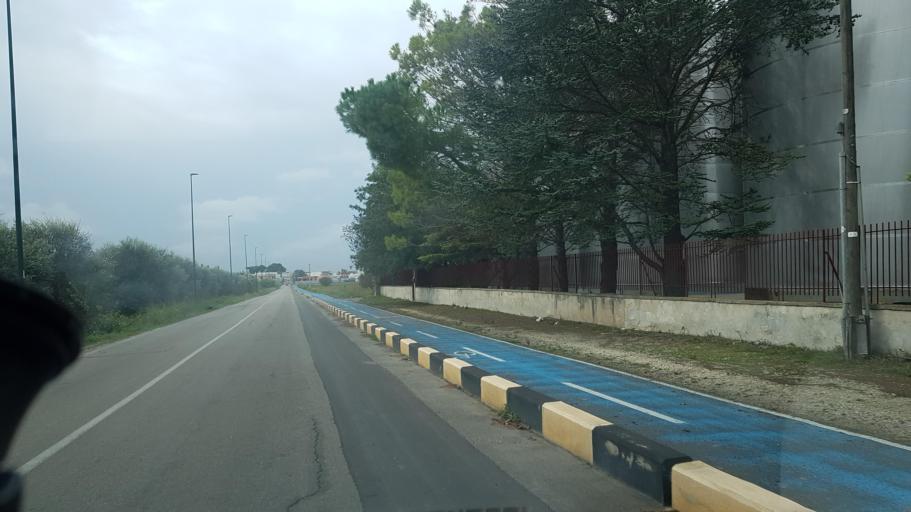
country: IT
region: Apulia
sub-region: Provincia di Lecce
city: Guagnano
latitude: 40.4092
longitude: 17.9562
